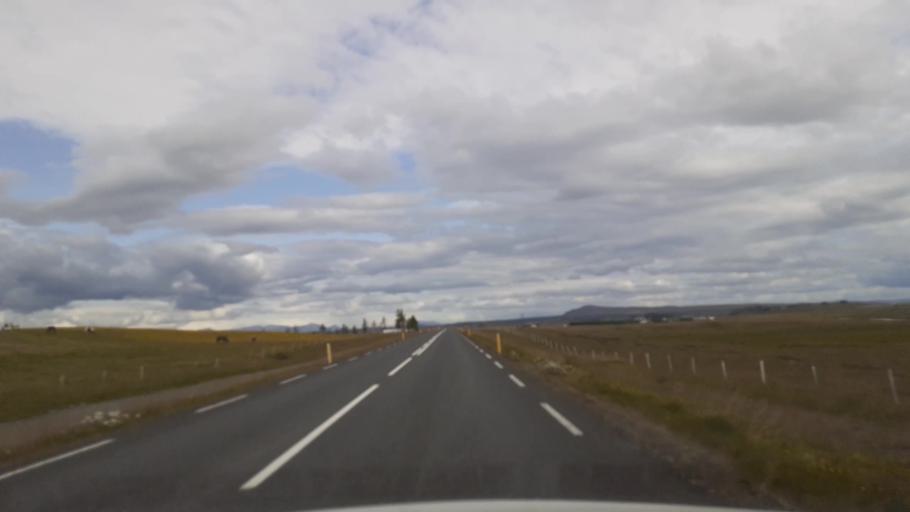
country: IS
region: South
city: Selfoss
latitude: 63.9292
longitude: -20.8469
